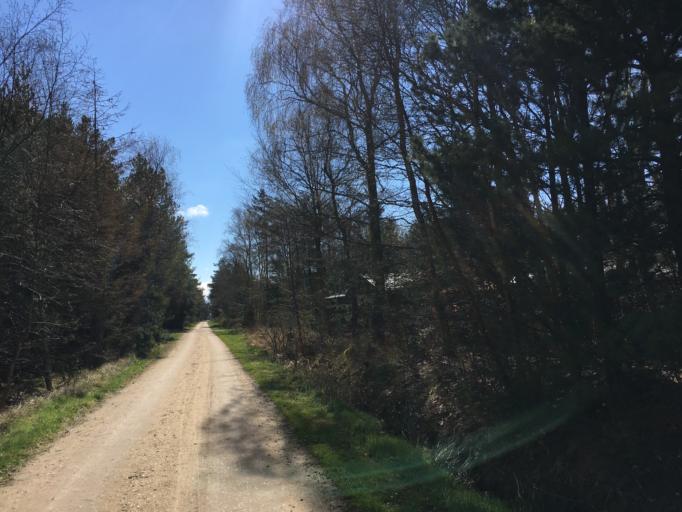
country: DK
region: South Denmark
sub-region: Varde Kommune
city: Oksbol
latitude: 55.5606
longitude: 8.2210
